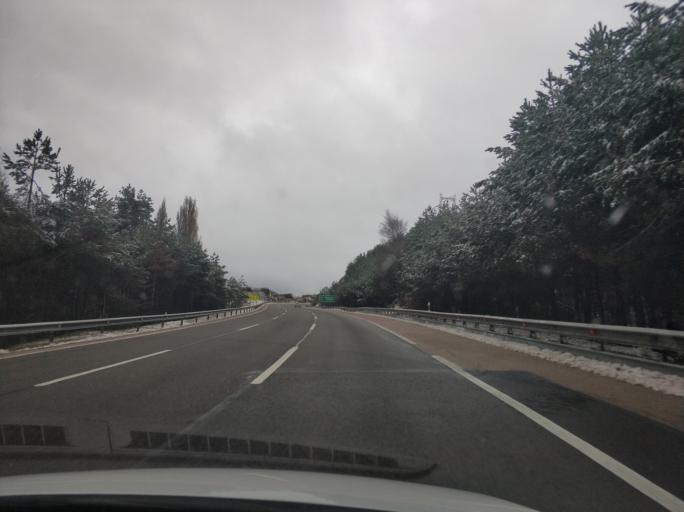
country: ES
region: Madrid
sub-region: Provincia de Madrid
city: Somosierra
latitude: 41.1619
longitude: -3.5853
